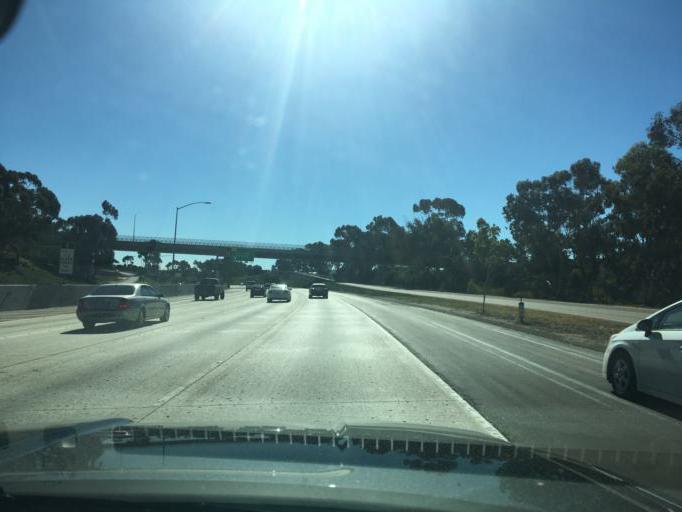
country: US
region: California
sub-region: San Diego County
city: National City
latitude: 32.7172
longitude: -117.1034
